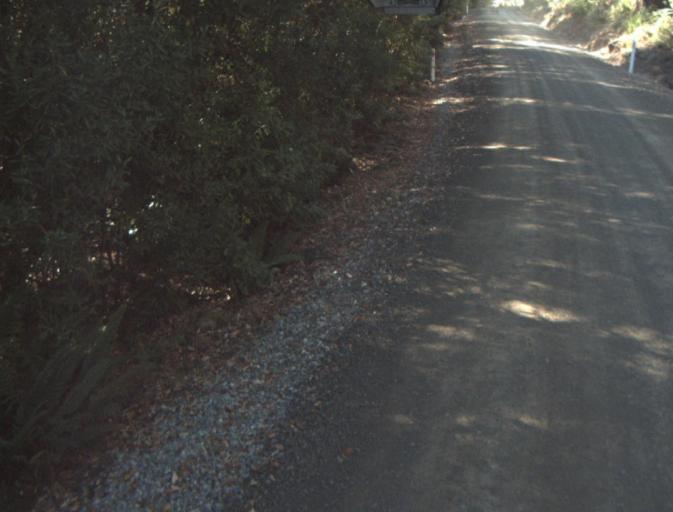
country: AU
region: Tasmania
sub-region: Launceston
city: Mayfield
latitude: -41.3015
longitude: 147.1904
